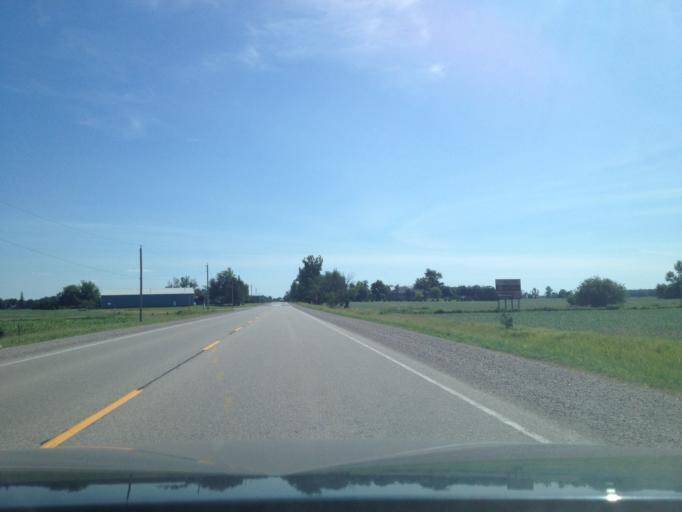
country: CA
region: Ontario
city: Stratford
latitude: 43.4914
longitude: -80.8853
